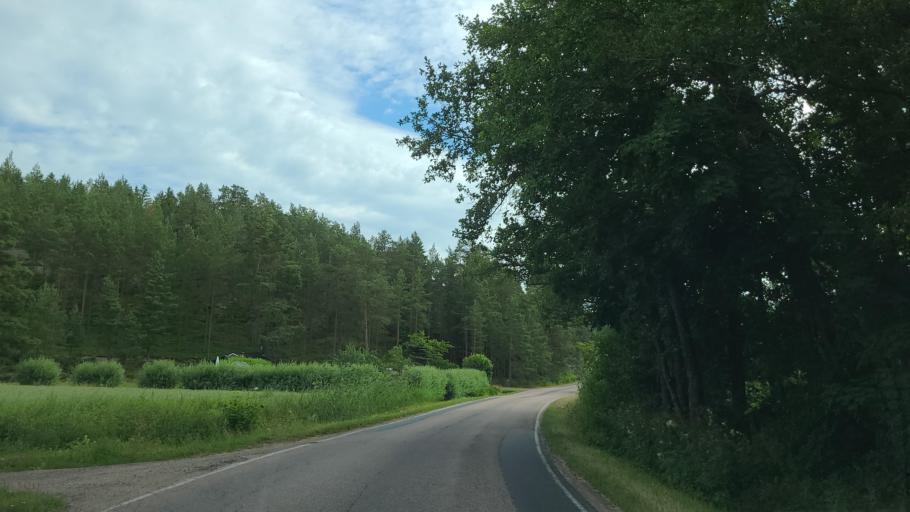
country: FI
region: Varsinais-Suomi
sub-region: Turku
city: Rymaettylae
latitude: 60.3440
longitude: 21.9785
